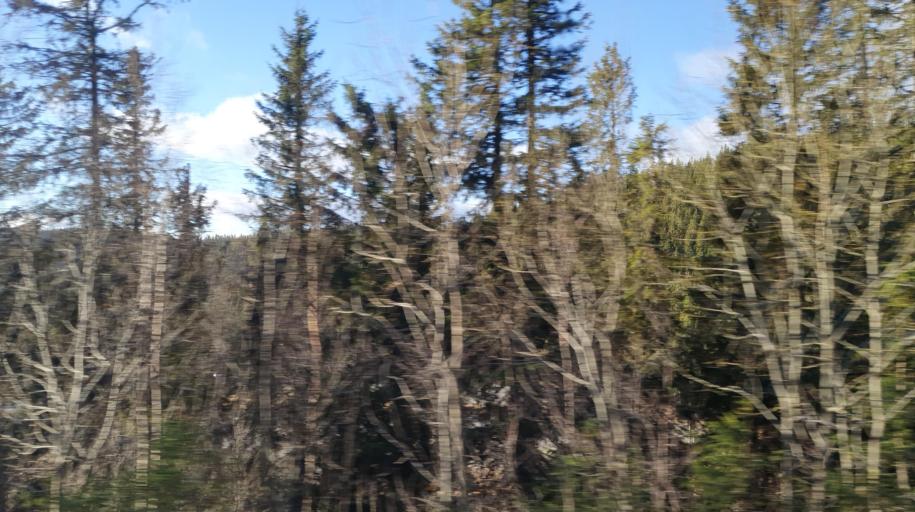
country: NO
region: Buskerud
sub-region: Krodsherad
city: Noresund
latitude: 60.2216
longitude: 9.5329
